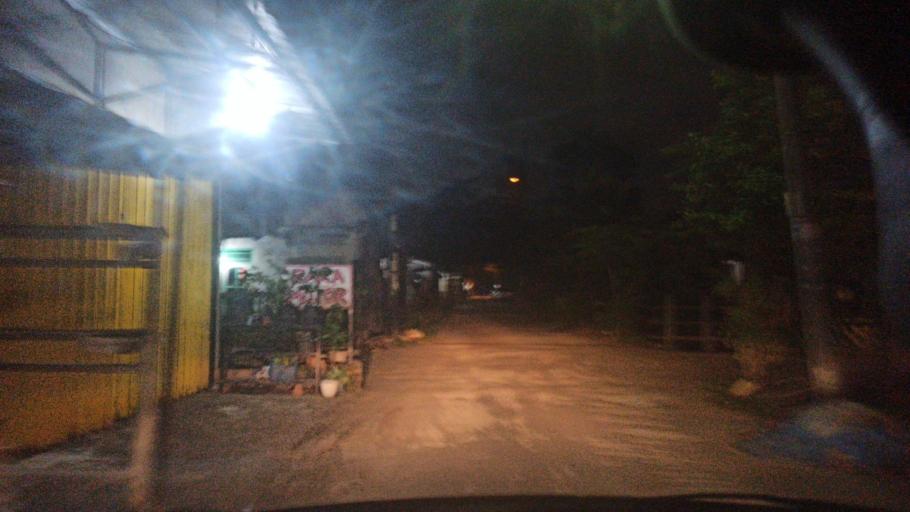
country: ID
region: South Sumatra
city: Palembang
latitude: -2.9252
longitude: 104.7957
